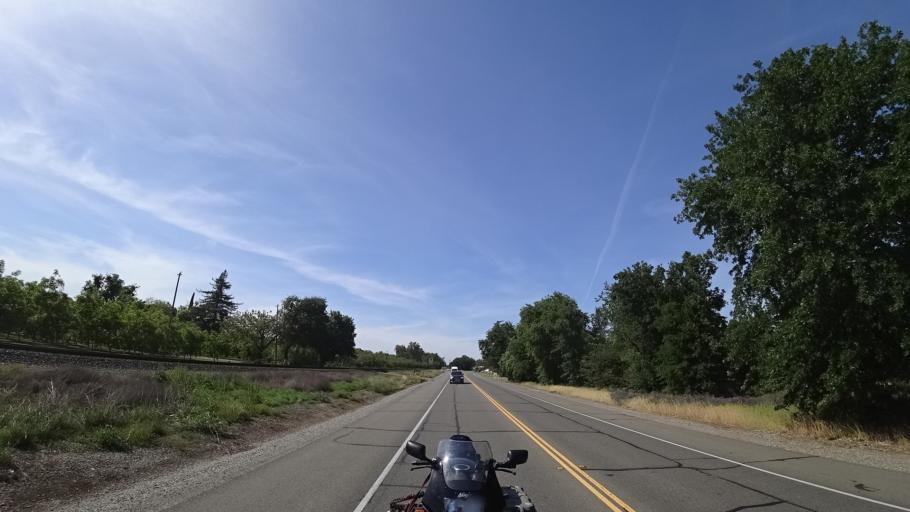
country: US
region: California
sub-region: Tehama County
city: Los Molinos
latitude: 40.0177
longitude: -122.0984
